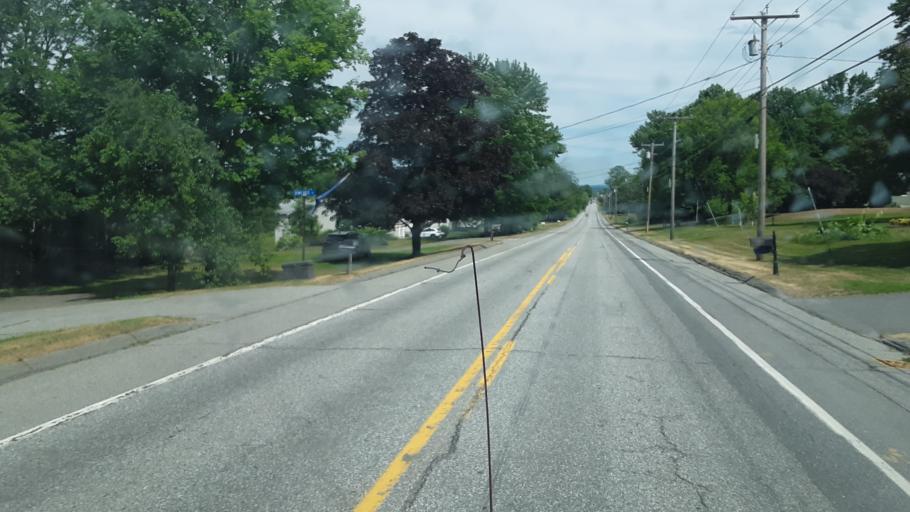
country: US
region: Maine
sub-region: Somerset County
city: Fairfield
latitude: 44.5975
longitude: -69.6380
